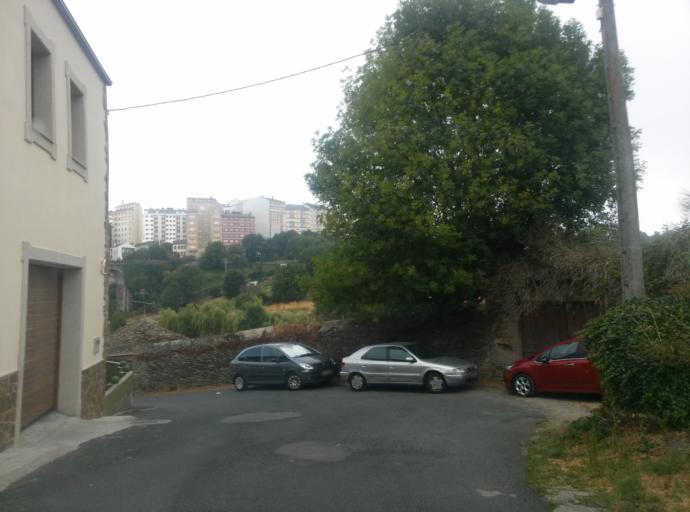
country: ES
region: Galicia
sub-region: Provincia de Lugo
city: Lugo
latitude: 43.0137
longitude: -7.5452
